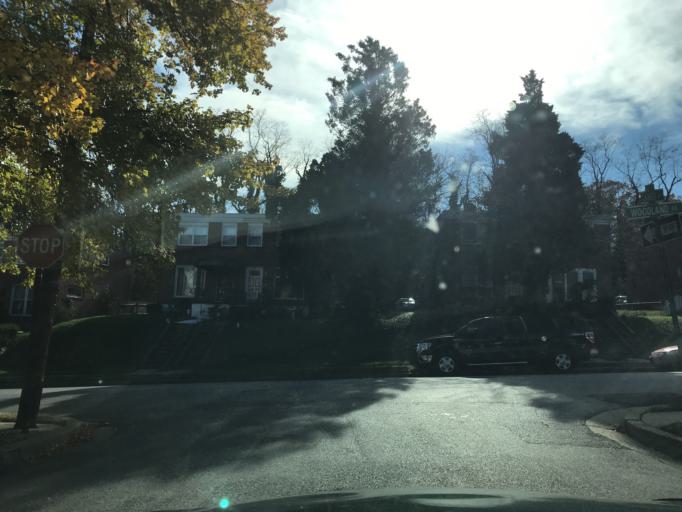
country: US
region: Maryland
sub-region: Baltimore County
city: Lochearn
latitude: 39.3469
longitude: -76.6619
